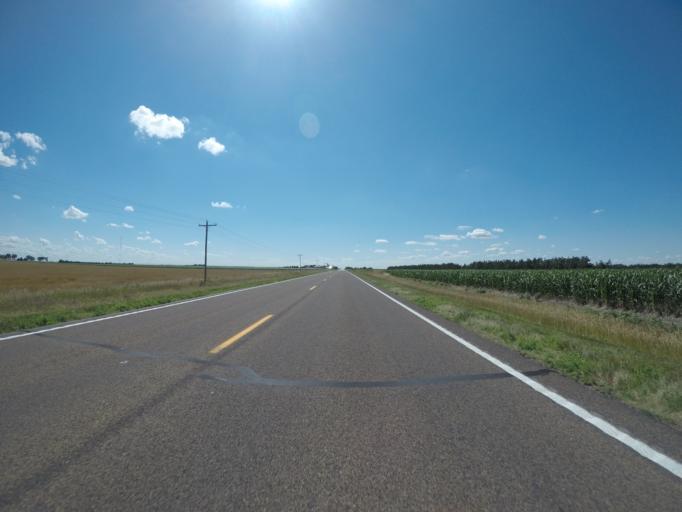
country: US
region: Nebraska
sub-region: Chase County
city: Imperial
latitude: 40.5376
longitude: -101.6560
